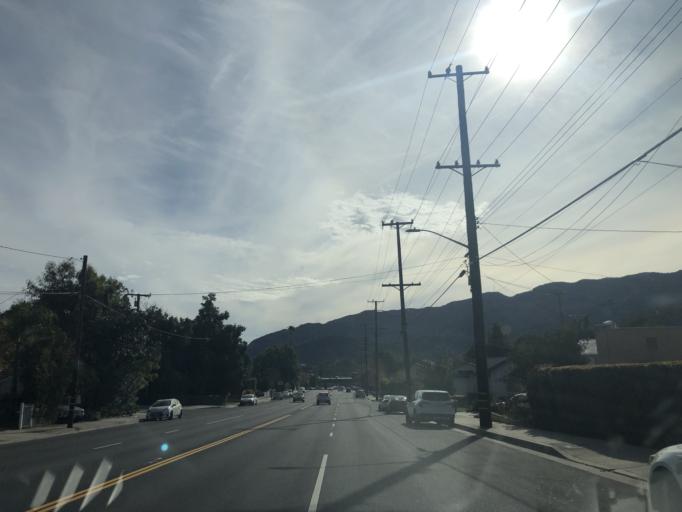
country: US
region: California
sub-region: Los Angeles County
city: La Crescenta-Montrose
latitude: 34.2274
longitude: -118.2484
